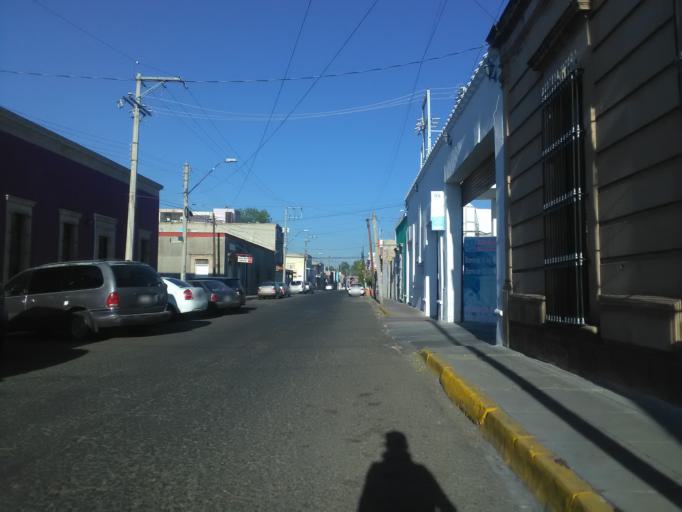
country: MX
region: Durango
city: Victoria de Durango
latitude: 24.0340
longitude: -104.6769
